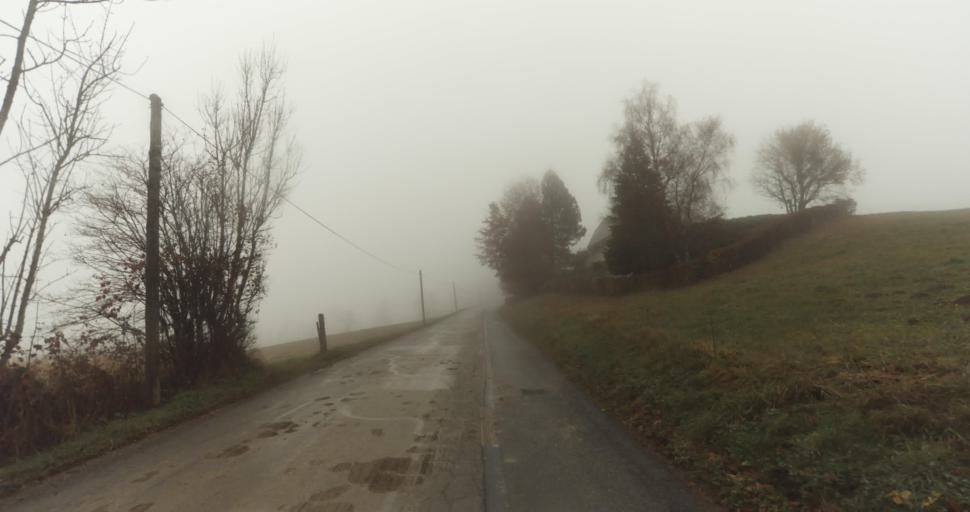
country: FR
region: Rhone-Alpes
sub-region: Departement de la Haute-Savoie
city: Villaz
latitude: 45.9787
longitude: 6.1874
